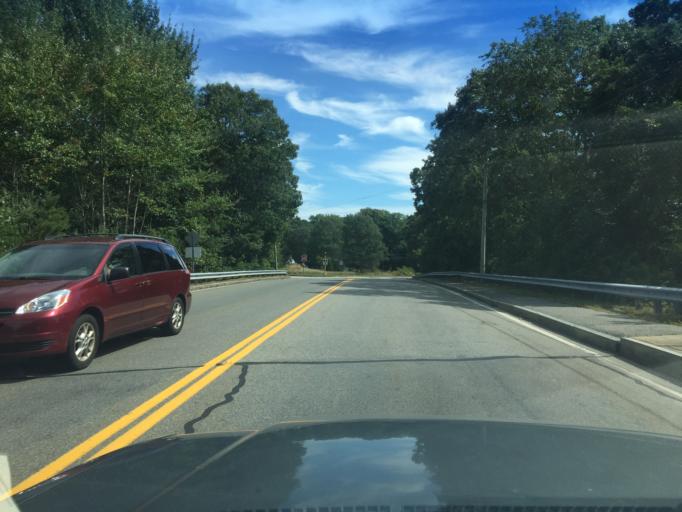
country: US
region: Massachusetts
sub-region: Barnstable County
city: North Falmouth
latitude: 41.6337
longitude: -70.6196
